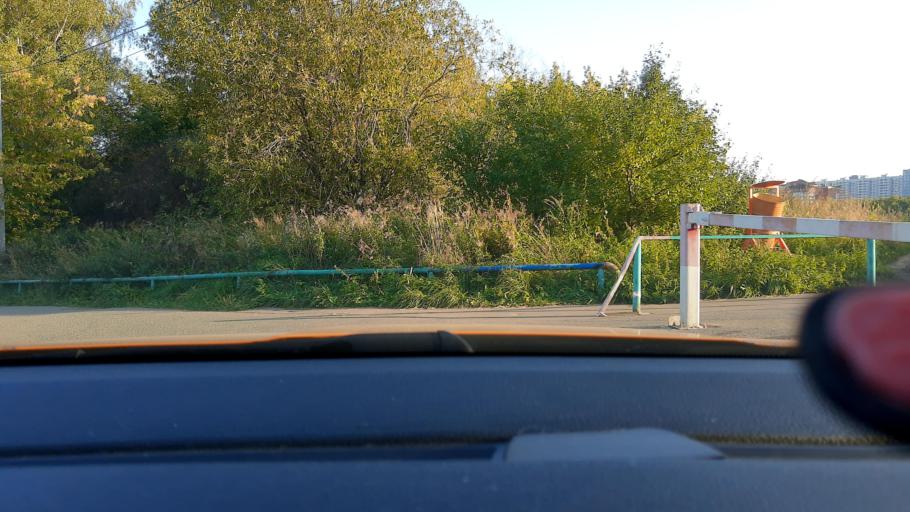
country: RU
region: Moskovskaya
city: Bol'shaya Setun'
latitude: 55.7559
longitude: 37.4230
